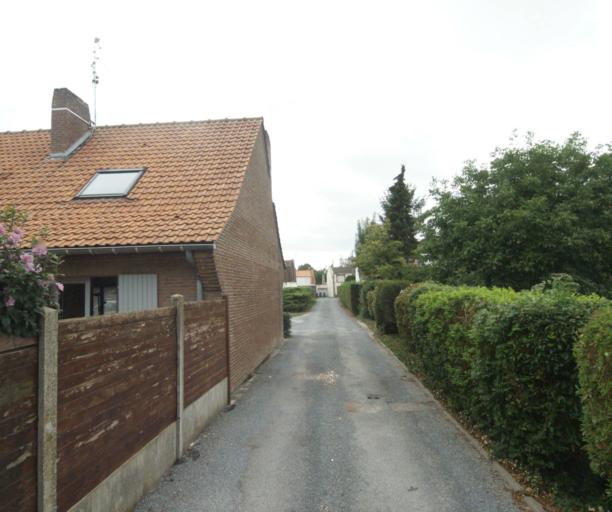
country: FR
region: Nord-Pas-de-Calais
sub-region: Departement du Nord
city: Toufflers
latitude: 50.6733
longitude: 3.2290
